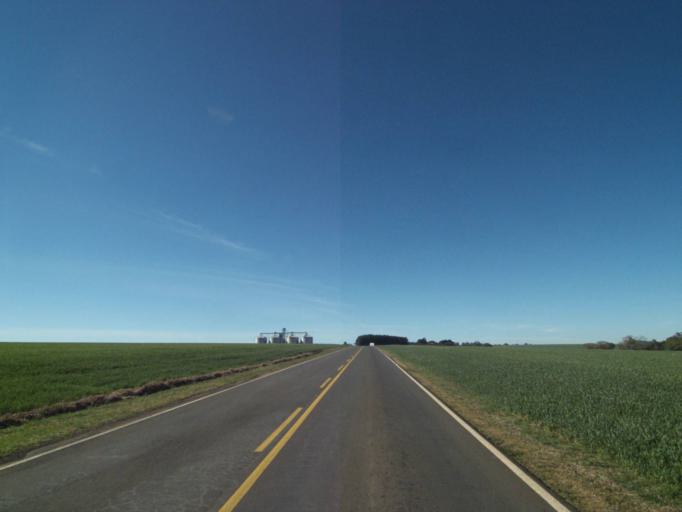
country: BR
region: Parana
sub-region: Tibagi
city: Tibagi
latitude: -24.5386
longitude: -50.3107
